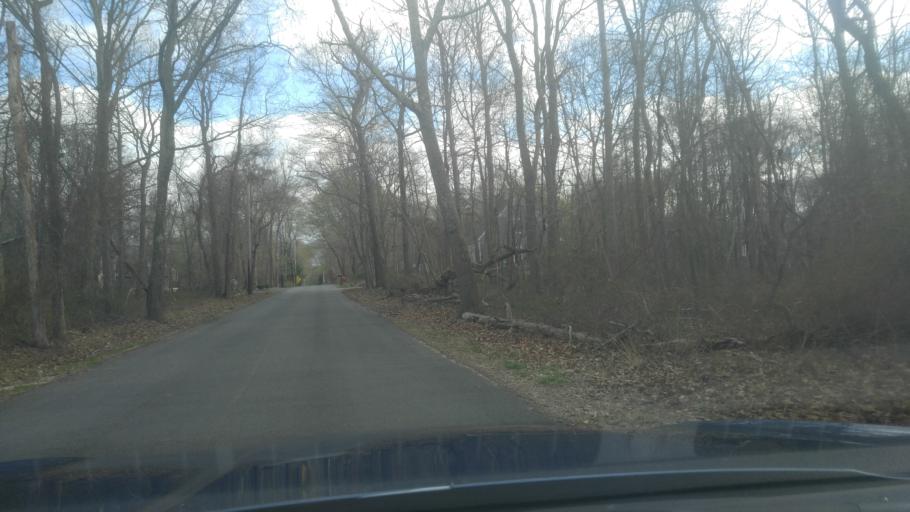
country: US
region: Rhode Island
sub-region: Newport County
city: Jamestown
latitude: 41.5672
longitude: -71.3725
